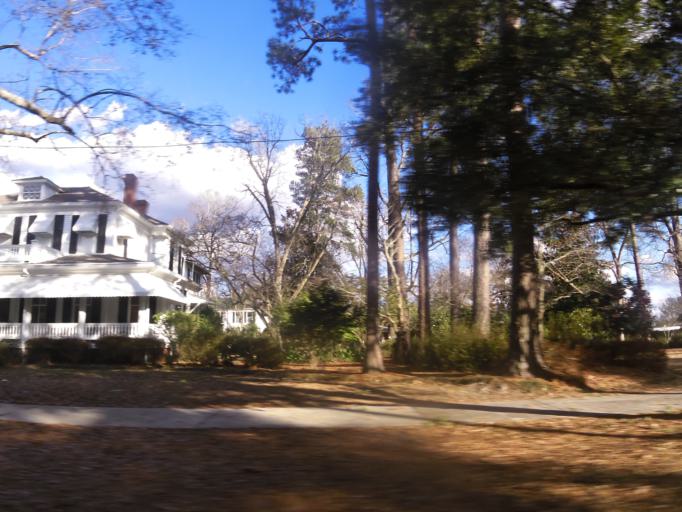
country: US
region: South Carolina
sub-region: Clarendon County
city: Manning
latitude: 33.6989
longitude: -80.2106
